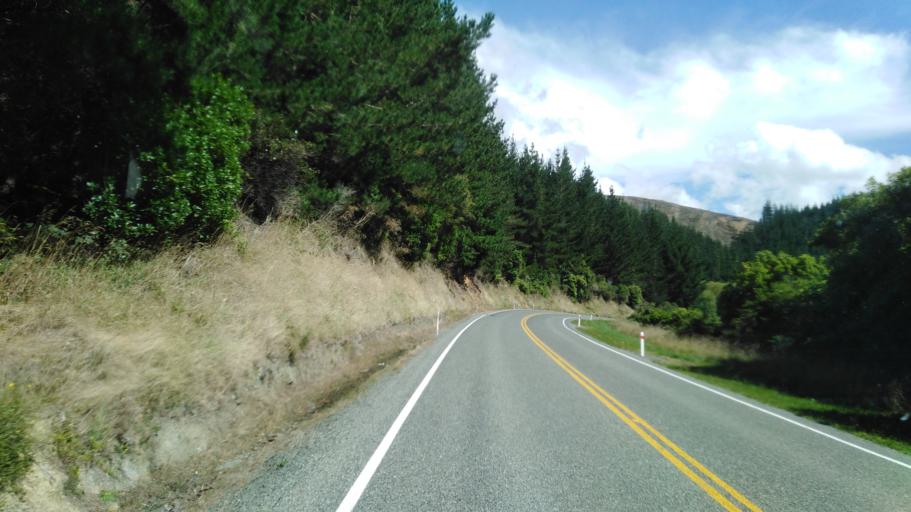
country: NZ
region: Nelson
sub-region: Nelson City
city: Nelson
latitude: -41.1609
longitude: 173.5266
